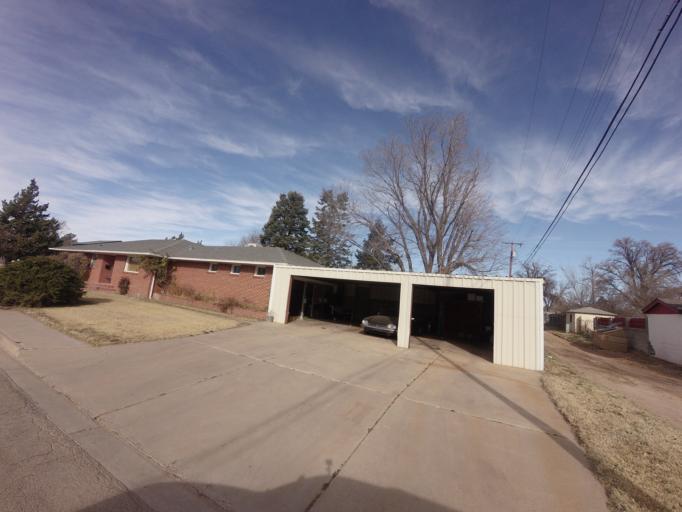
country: US
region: New Mexico
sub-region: Curry County
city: Clovis
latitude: 34.4173
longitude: -103.2010
